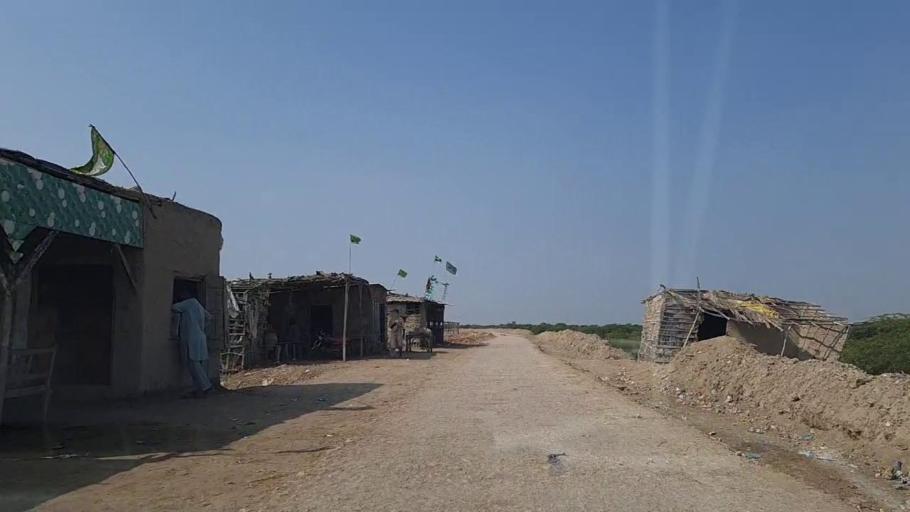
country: PK
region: Sindh
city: Chuhar Jamali
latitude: 24.1962
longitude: 67.8375
